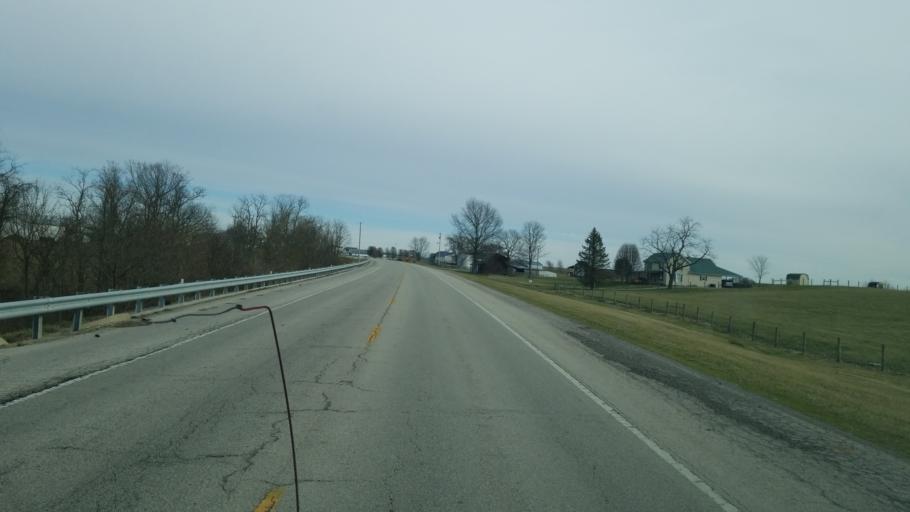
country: US
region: Kentucky
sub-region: Fleming County
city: Flemingsburg
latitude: 38.4782
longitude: -83.8812
